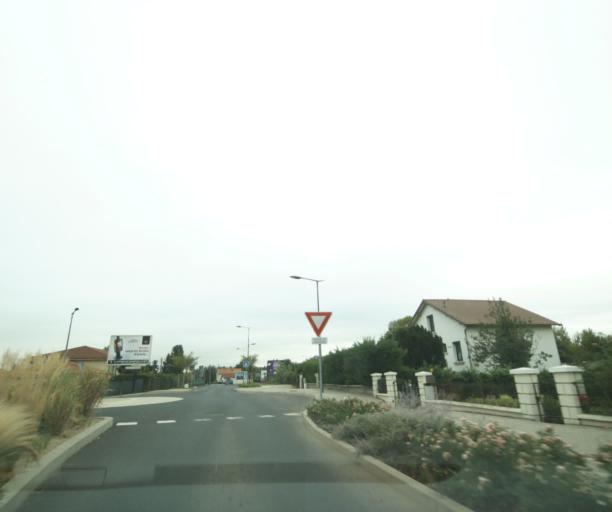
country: FR
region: Auvergne
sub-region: Departement du Puy-de-Dome
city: Gerzat
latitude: 45.8172
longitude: 3.1407
